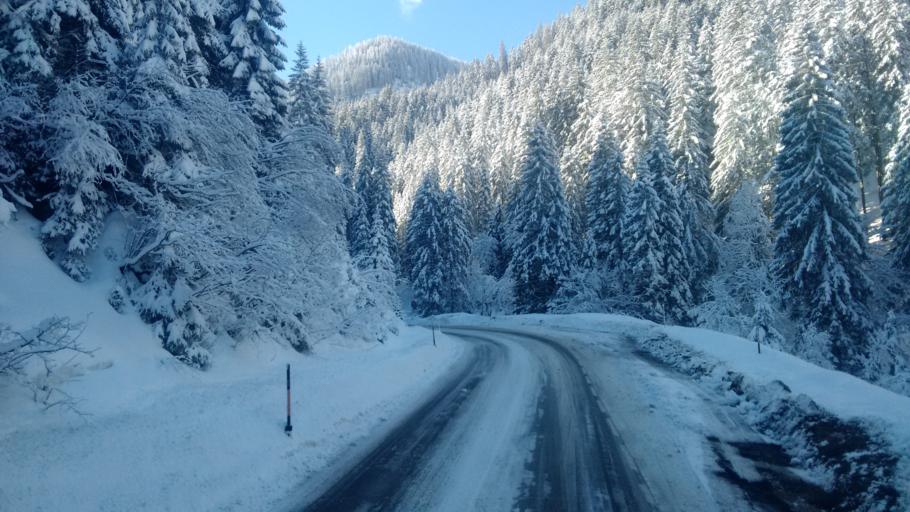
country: AT
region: Salzburg
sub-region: Politischer Bezirk Sankt Johann im Pongau
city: Untertauern
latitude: 47.3104
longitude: 13.4492
